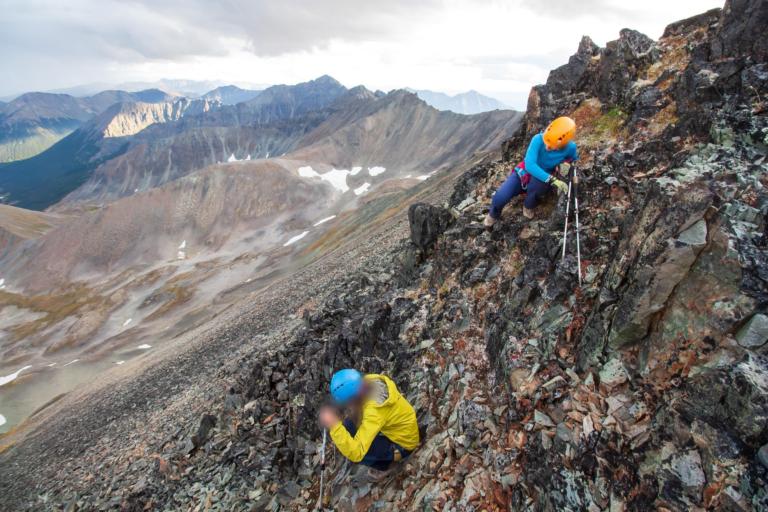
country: RU
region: Kamtsjatka
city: Yelizovo
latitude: 53.8681
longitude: 158.2351
